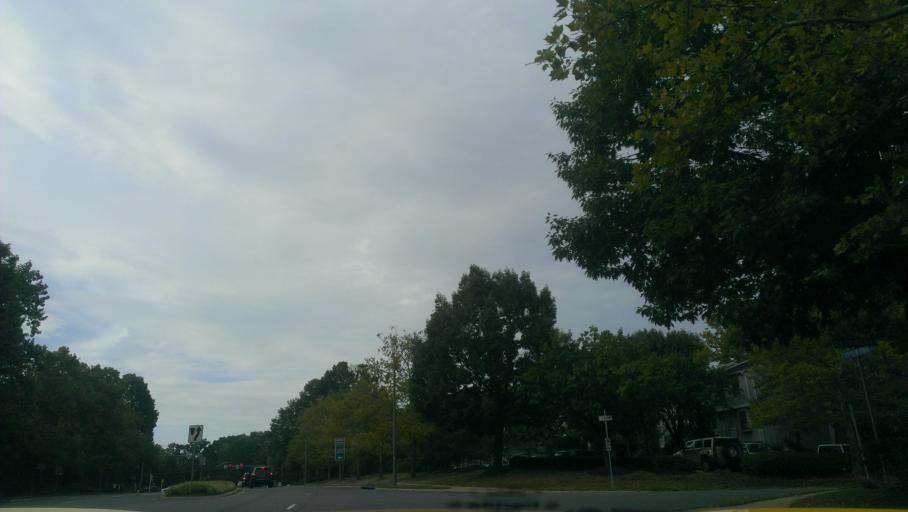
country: US
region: Virginia
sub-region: Fairfax County
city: Merrifield
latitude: 38.8738
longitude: -77.2154
